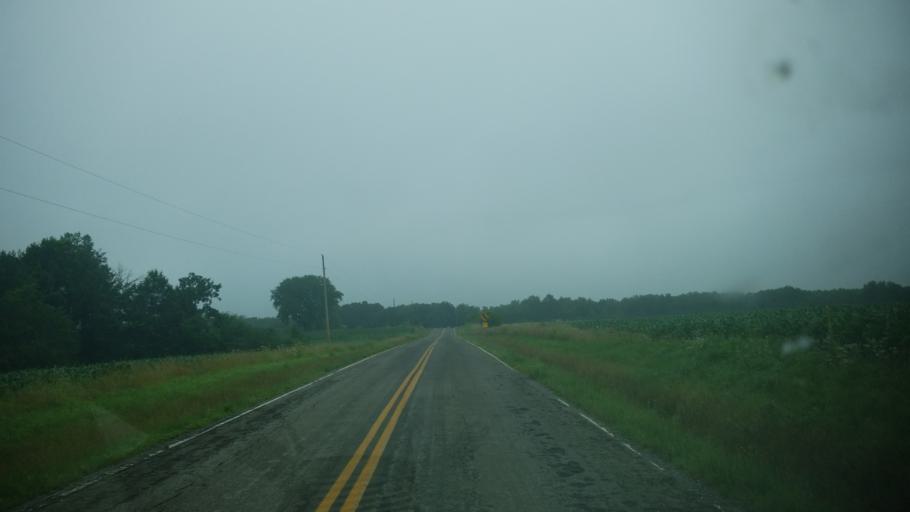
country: US
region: Missouri
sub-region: Audrain County
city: Vandalia
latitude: 39.2845
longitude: -91.3461
